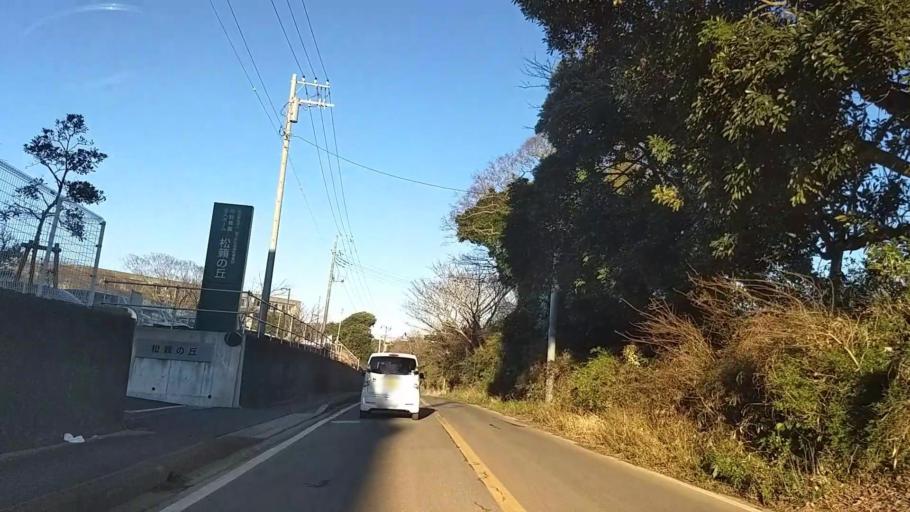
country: JP
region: Chiba
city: Hasaki
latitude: 35.7600
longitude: 140.7486
